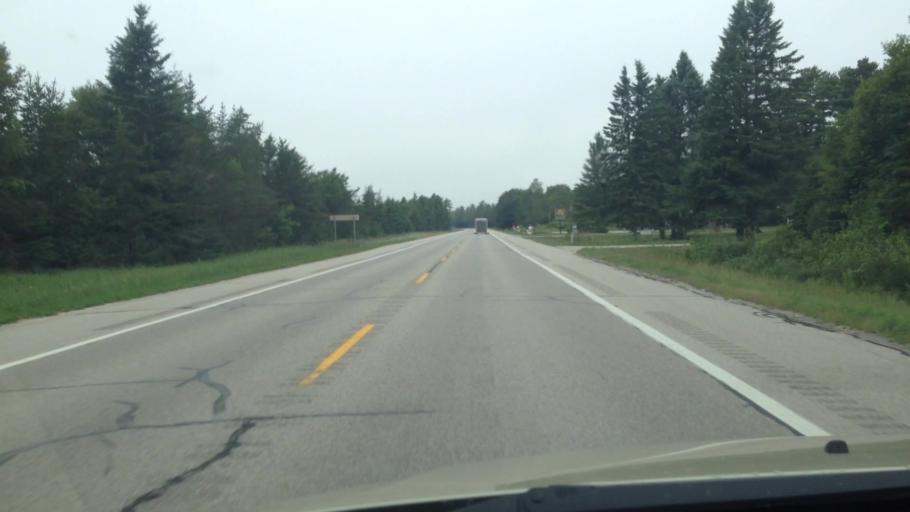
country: US
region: Michigan
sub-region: Luce County
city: Newberry
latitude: 46.0899
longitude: -85.3229
